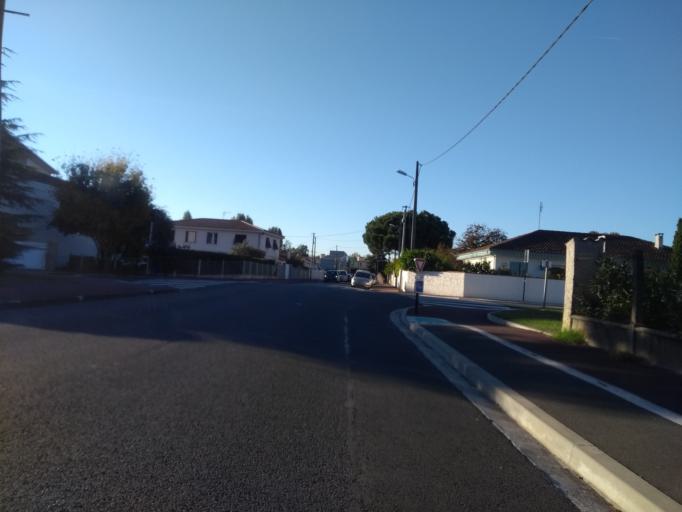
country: FR
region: Aquitaine
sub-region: Departement de la Gironde
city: Gradignan
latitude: 44.7805
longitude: -0.6034
